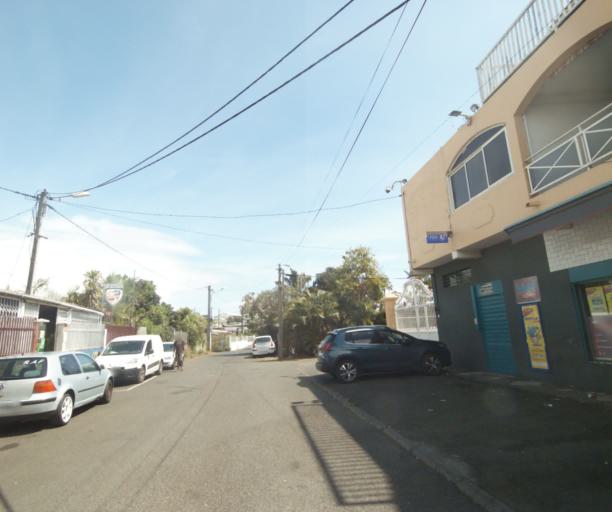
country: RE
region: Reunion
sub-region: Reunion
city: Saint-Paul
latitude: -21.0574
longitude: 55.2602
